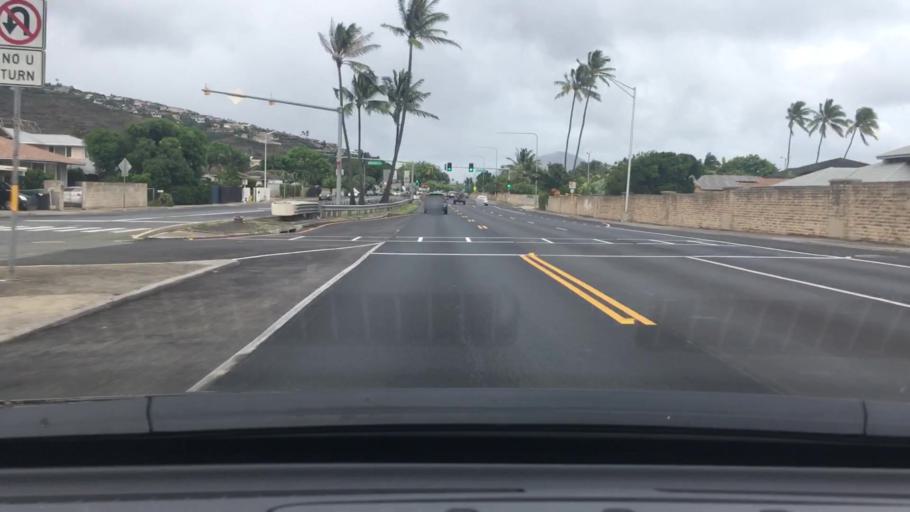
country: US
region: Hawaii
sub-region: Honolulu County
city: Waimanalo
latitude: 21.2769
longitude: -157.7587
